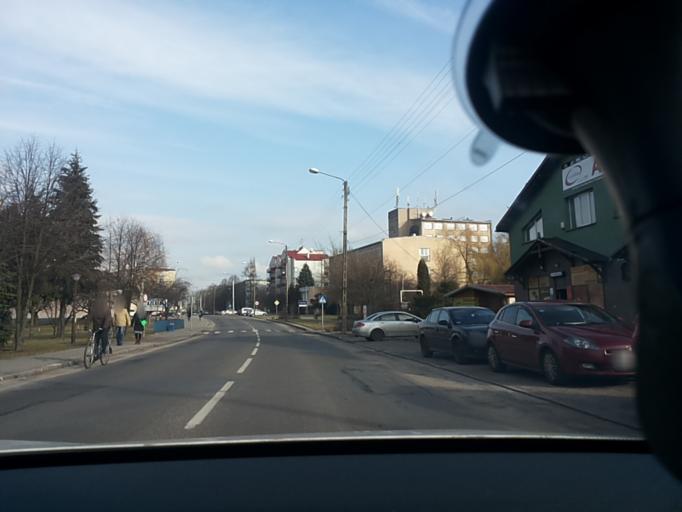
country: PL
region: Lodz Voivodeship
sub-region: Skierniewice
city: Skierniewice
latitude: 51.9596
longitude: 20.1481
